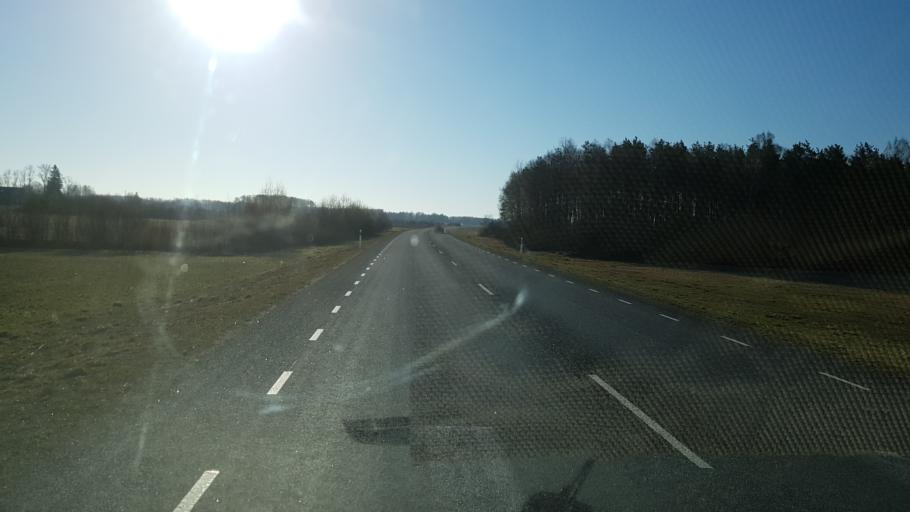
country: EE
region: Jaervamaa
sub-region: Tueri vald
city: Sarevere
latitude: 58.7771
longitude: 25.5032
